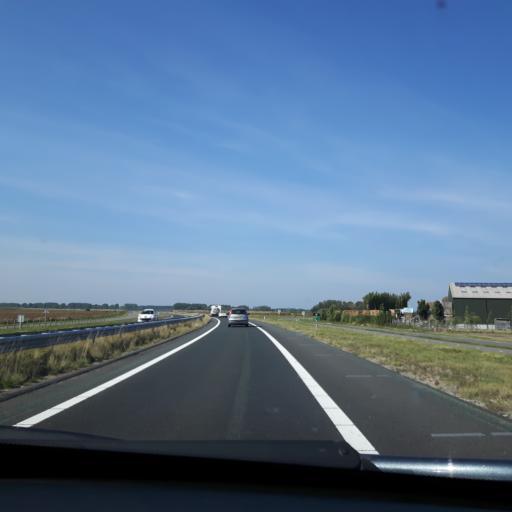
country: NL
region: Zeeland
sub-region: Gemeente Vlissingen
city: Vlissingen
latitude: 51.3382
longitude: 3.5723
